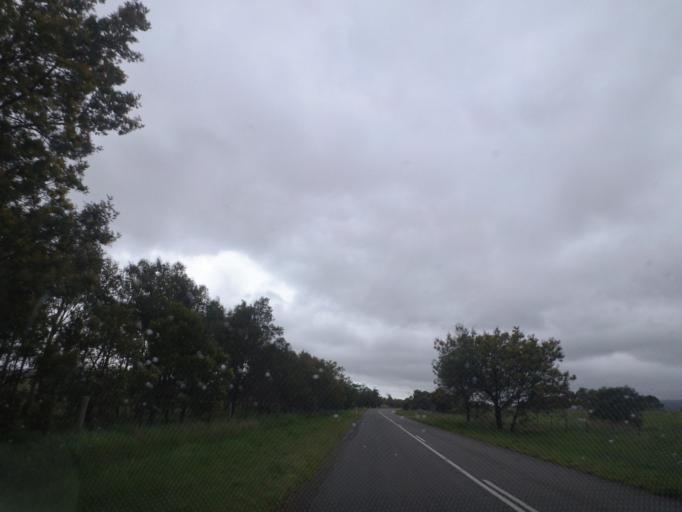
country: AU
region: Victoria
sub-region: Hume
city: Sunbury
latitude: -37.3215
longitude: 144.5389
